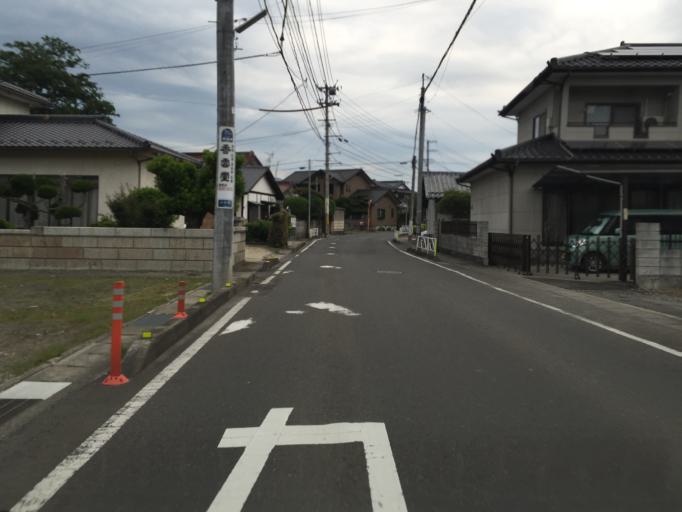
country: JP
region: Fukushima
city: Hobaramachi
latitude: 37.8120
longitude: 140.4955
